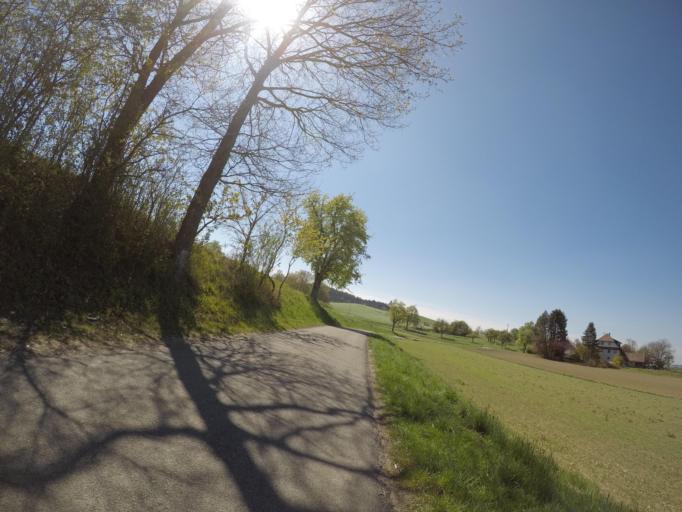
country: DE
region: Baden-Wuerttemberg
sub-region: Tuebingen Region
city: Markdorf
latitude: 47.7552
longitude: 9.3978
